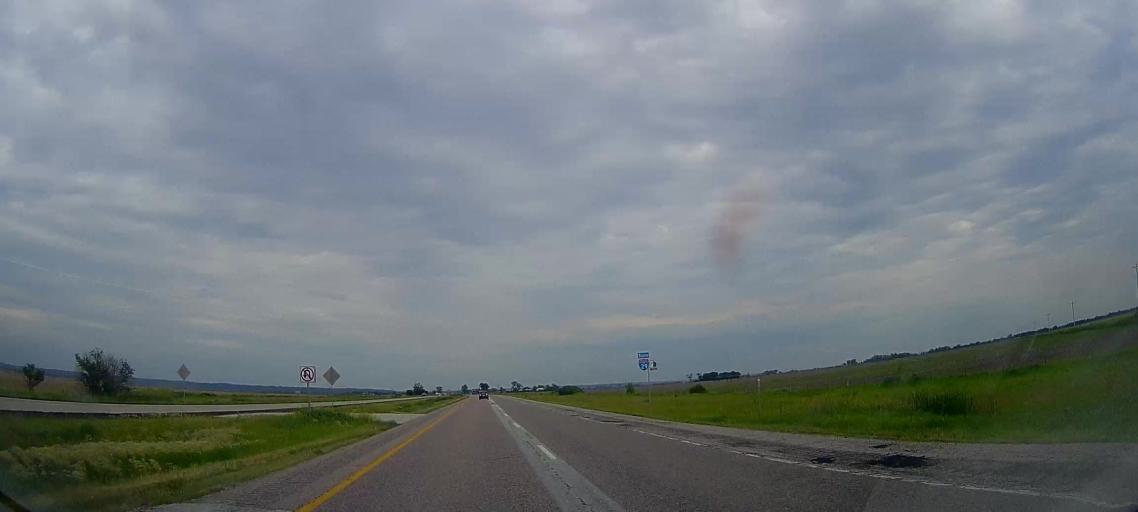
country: US
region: Iowa
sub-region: Harrison County
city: Missouri Valley
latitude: 41.6150
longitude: -95.9820
